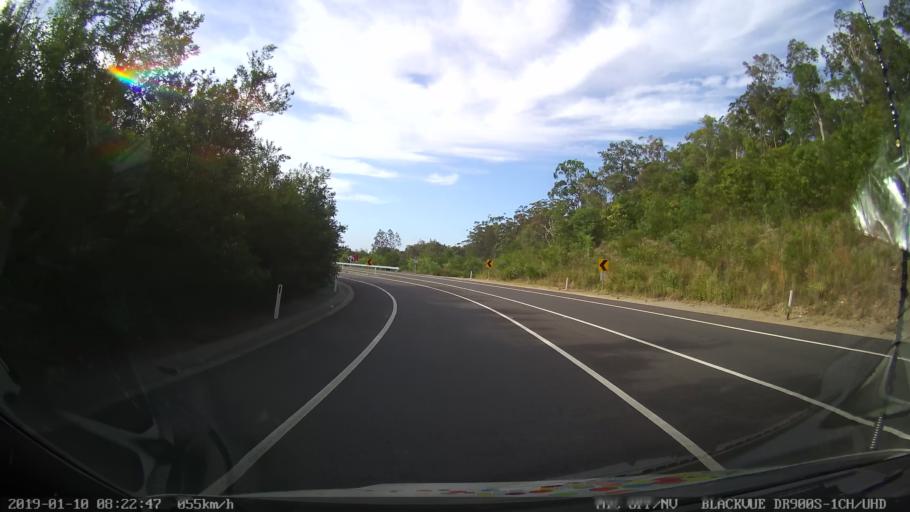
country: AU
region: New South Wales
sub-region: Coffs Harbour
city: Bonville
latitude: -30.4649
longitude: 153.0007
